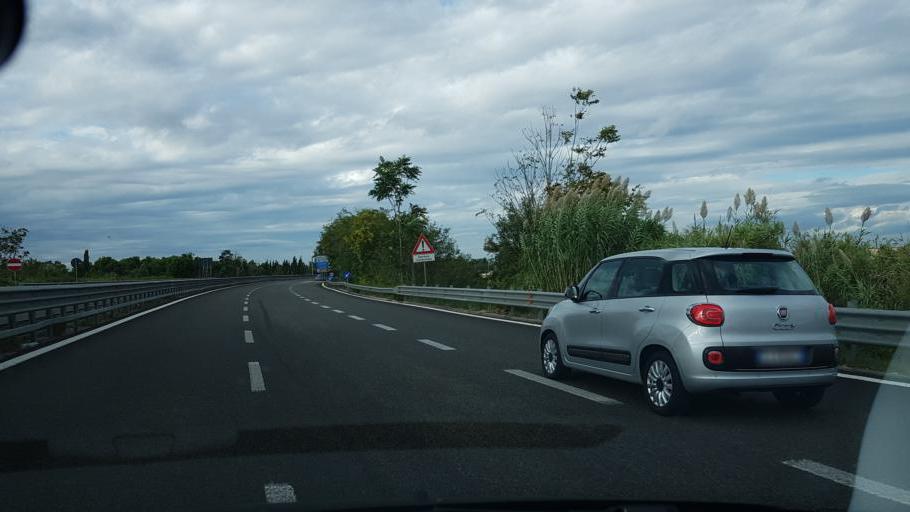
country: IT
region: Apulia
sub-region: Provincia di Lecce
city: Castromediano
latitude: 40.3233
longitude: 18.1859
